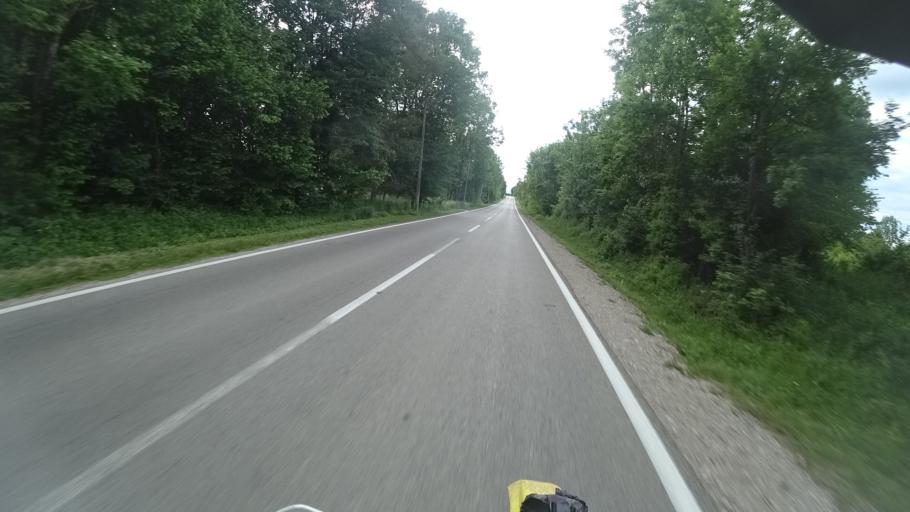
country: HR
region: Licko-Senjska
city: Gospic
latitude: 44.5072
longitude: 15.4417
